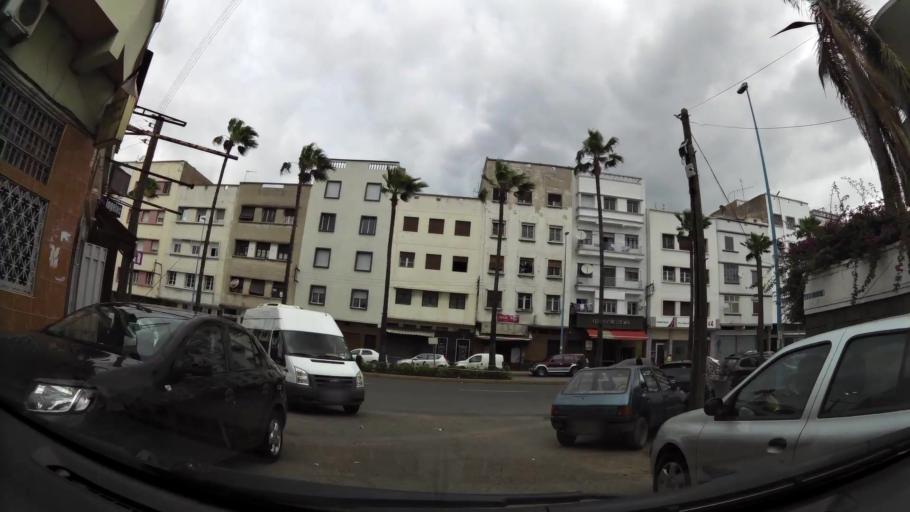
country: MA
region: Grand Casablanca
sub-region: Casablanca
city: Casablanca
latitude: 33.5619
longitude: -7.6104
